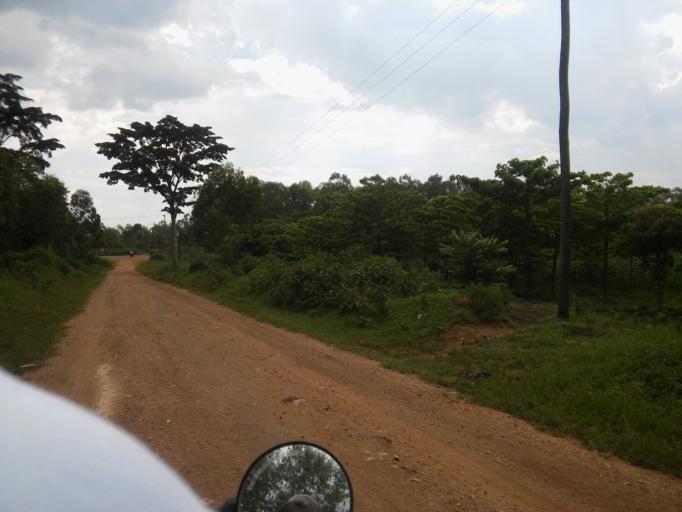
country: UG
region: Eastern Region
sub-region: Mbale District
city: Mbale
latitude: 1.0553
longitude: 34.1811
